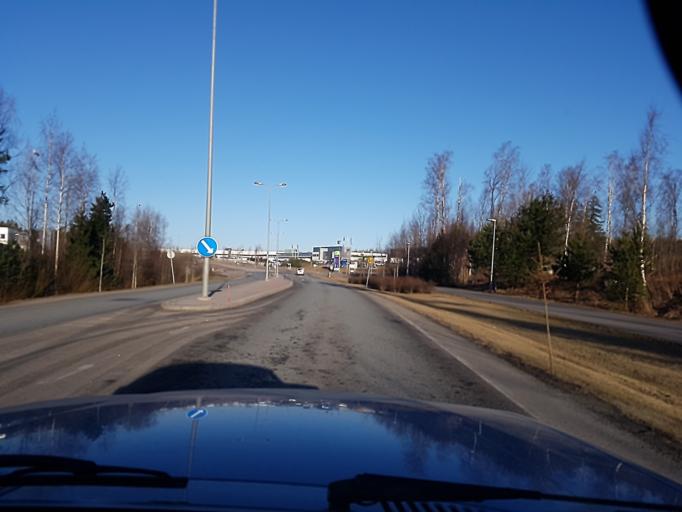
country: FI
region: Uusimaa
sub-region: Helsinki
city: Vantaa
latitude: 60.2940
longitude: 24.9260
